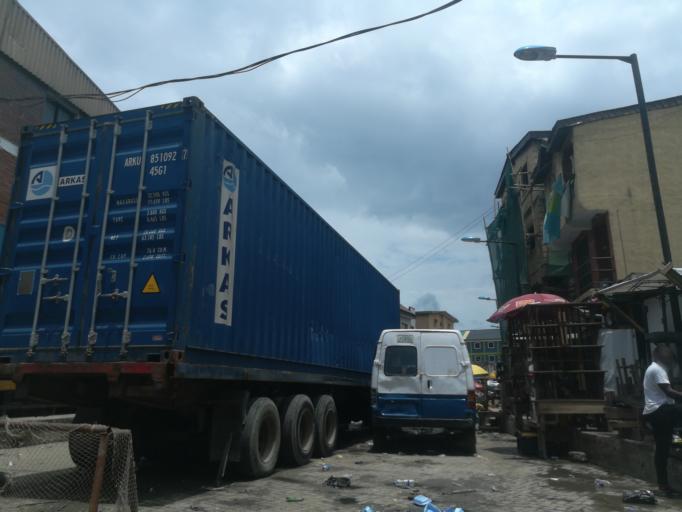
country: NG
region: Lagos
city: Lagos
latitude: 6.4596
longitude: 3.3839
